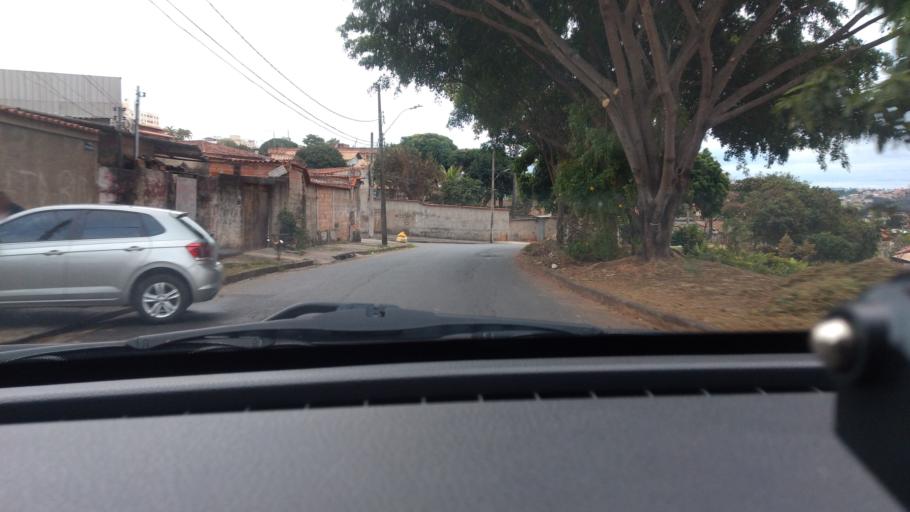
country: BR
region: Minas Gerais
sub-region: Belo Horizonte
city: Belo Horizonte
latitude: -19.8321
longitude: -43.9344
